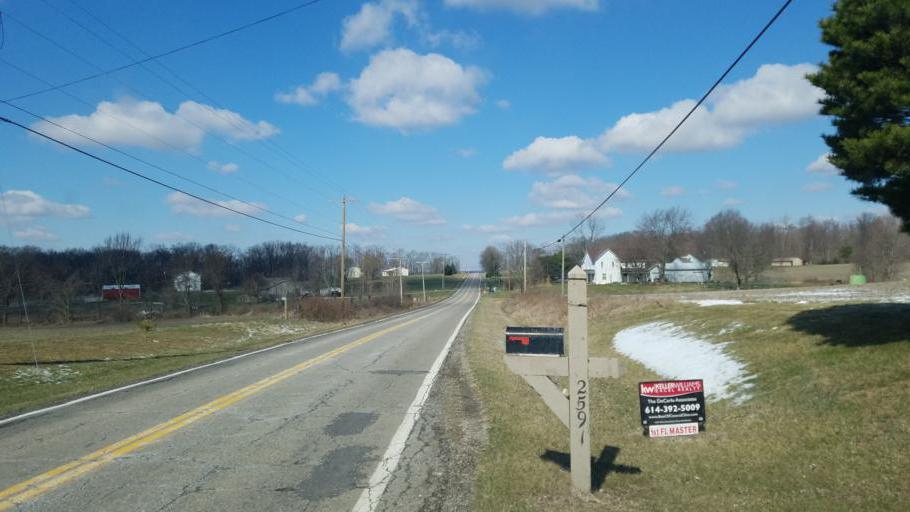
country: US
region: Ohio
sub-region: Licking County
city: Utica
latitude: 40.2418
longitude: -82.4848
